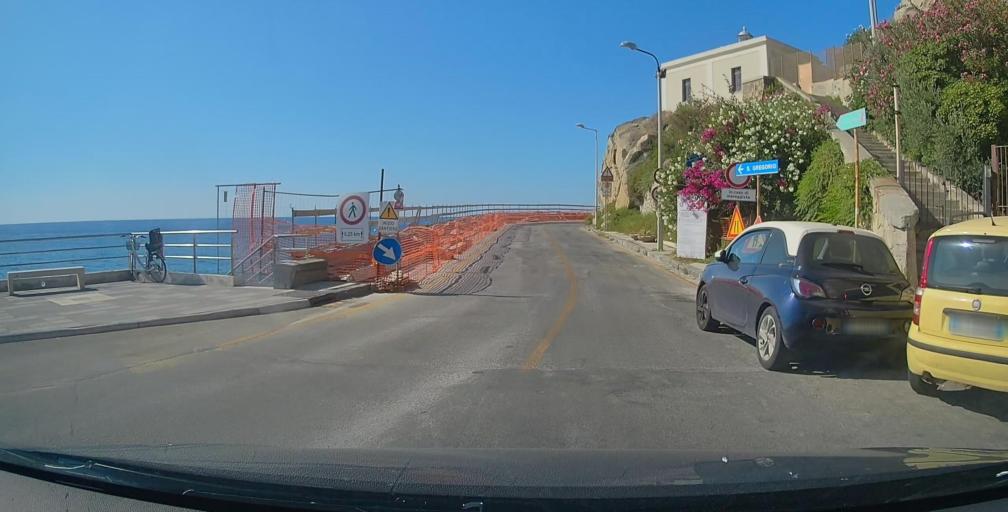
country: IT
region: Sicily
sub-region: Messina
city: Capo d'Orlando
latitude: 38.1642
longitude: 14.7469
